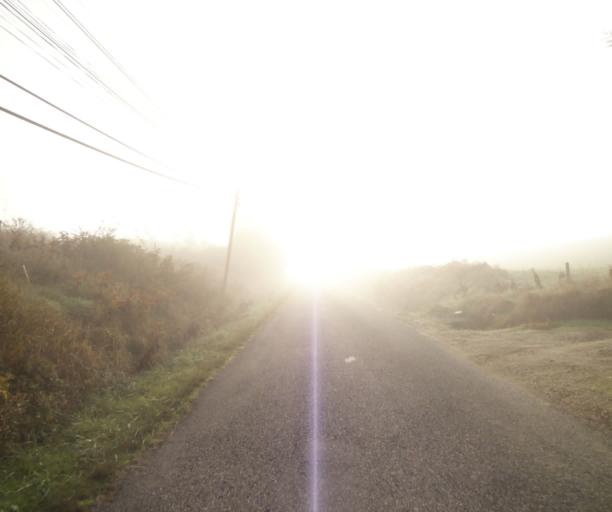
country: FR
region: Midi-Pyrenees
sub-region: Departement du Tarn-et-Garonne
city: Nohic
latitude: 43.9064
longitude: 1.4606
